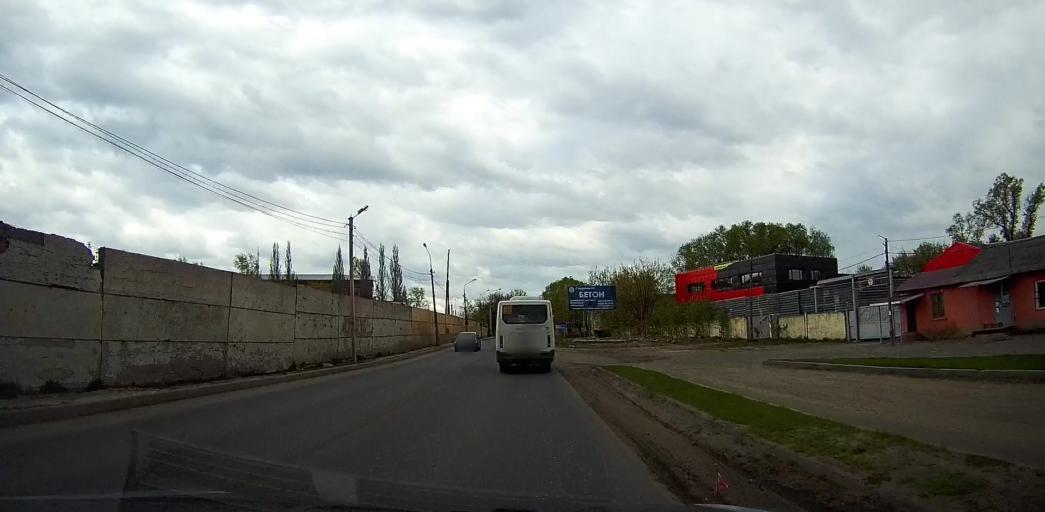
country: RU
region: Moskovskaya
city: Pavlovskiy Posad
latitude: 55.7786
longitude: 38.6873
